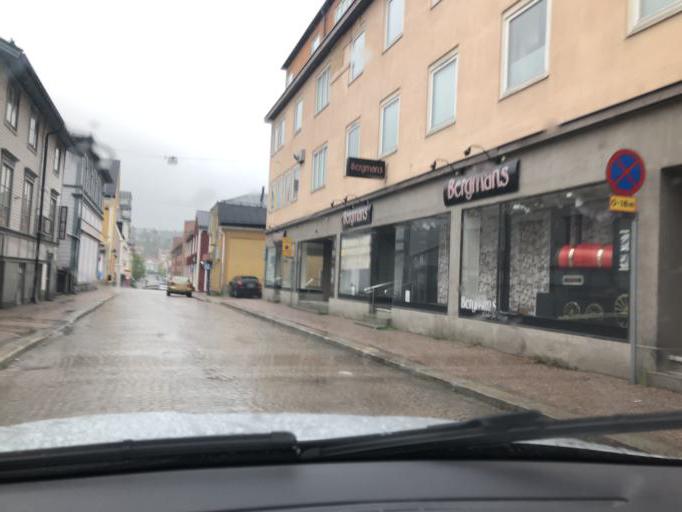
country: SE
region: Vaesternorrland
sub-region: OErnskoeldsviks Kommun
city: Ornskoldsvik
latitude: 63.2901
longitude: 18.7144
